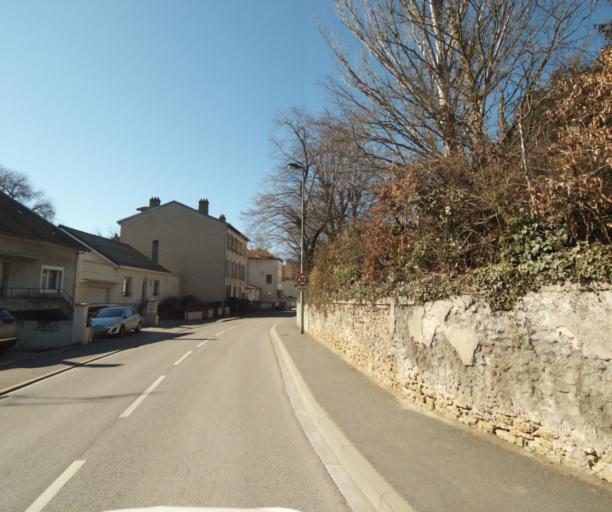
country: FR
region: Lorraine
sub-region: Departement de Meurthe-et-Moselle
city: Saint-Max
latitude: 48.7069
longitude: 6.2149
